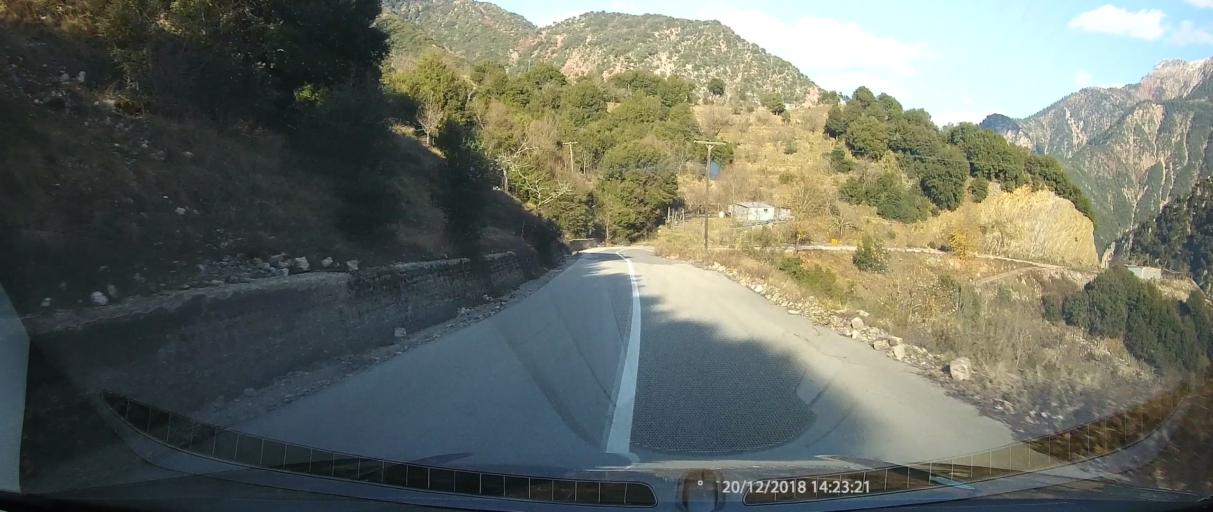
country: GR
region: West Greece
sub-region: Nomos Aitolias kai Akarnanias
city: Thermo
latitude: 38.7558
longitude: 21.6690
